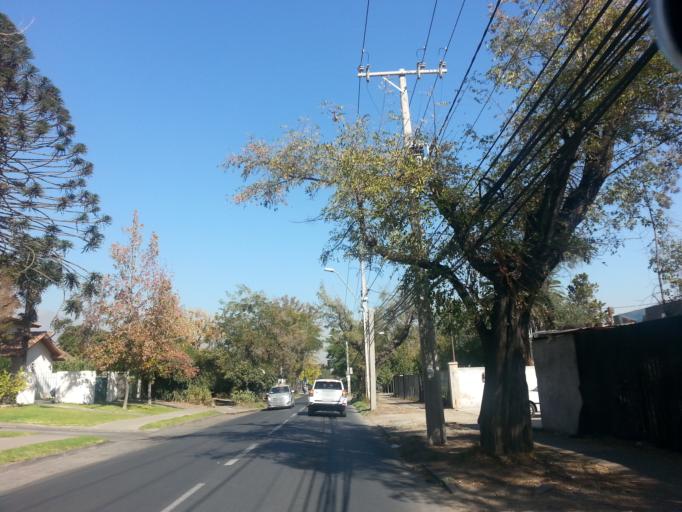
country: CL
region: Santiago Metropolitan
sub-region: Provincia de Santiago
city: Villa Presidente Frei, Nunoa, Santiago, Chile
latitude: -33.4433
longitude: -70.5434
